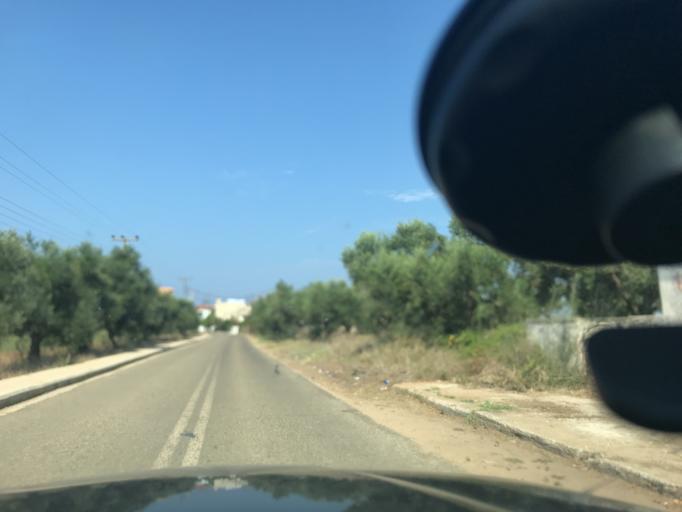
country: GR
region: West Greece
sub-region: Nomos Ileias
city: Kardamas
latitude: 37.7193
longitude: 21.3220
